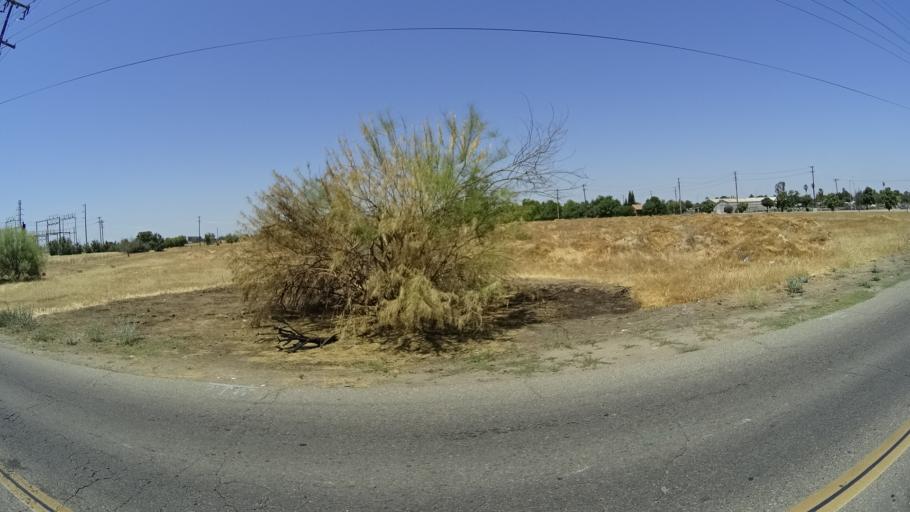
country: US
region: California
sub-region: Fresno County
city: West Park
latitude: 36.7204
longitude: -119.8177
